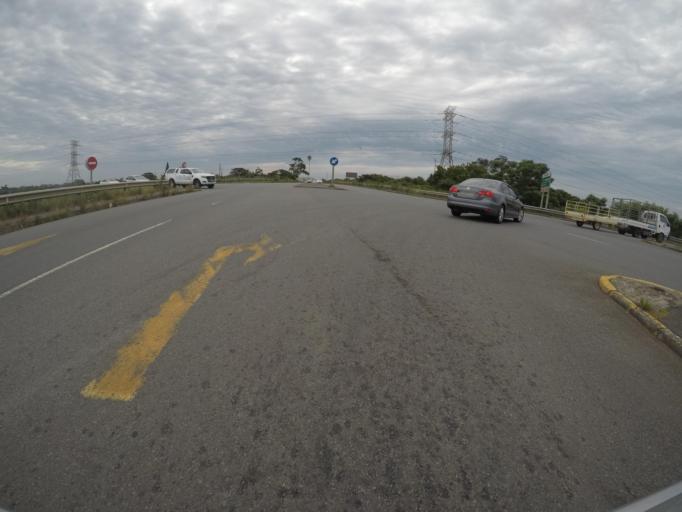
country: ZA
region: Eastern Cape
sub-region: Buffalo City Metropolitan Municipality
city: East London
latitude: -32.9697
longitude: 27.8496
